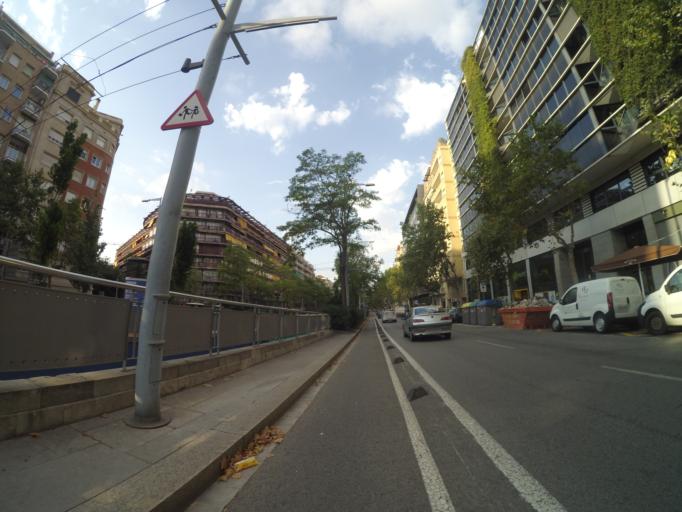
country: ES
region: Catalonia
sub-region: Provincia de Barcelona
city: Sarria-Sant Gervasi
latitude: 41.3903
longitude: 2.1434
